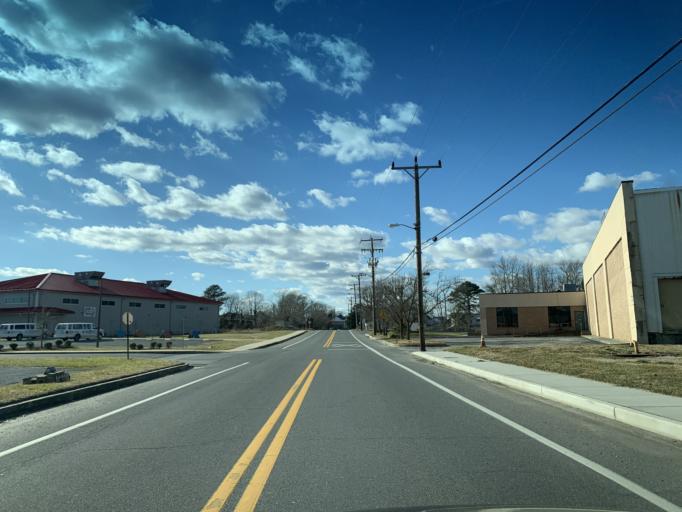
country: US
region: Maryland
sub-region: Worcester County
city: Berlin
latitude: 38.3339
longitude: -75.2177
